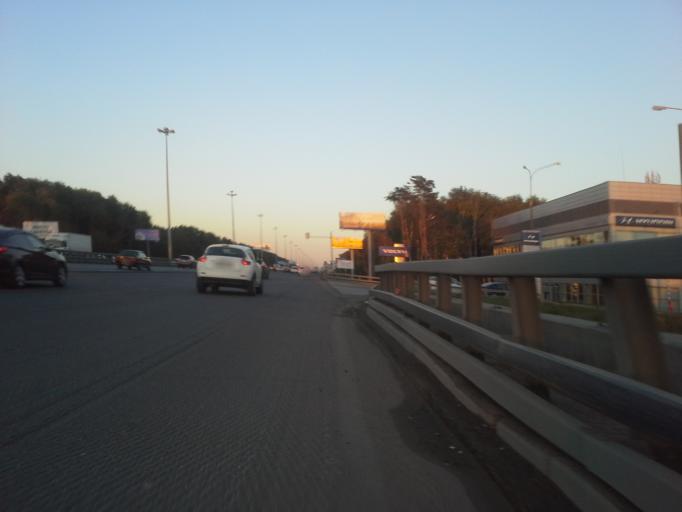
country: RU
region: Moscow
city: Solntsevo
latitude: 55.6194
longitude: 37.3946
